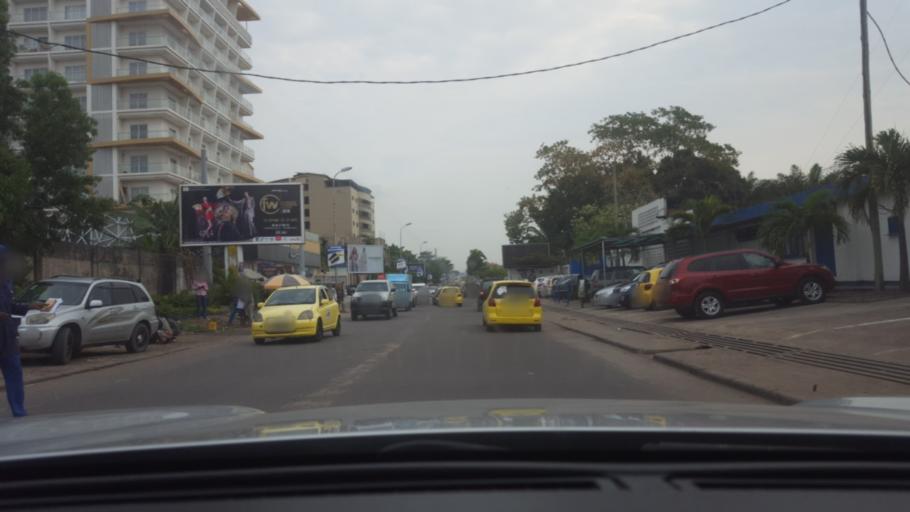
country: CD
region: Kinshasa
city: Kinshasa
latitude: -4.3245
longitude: 15.2772
